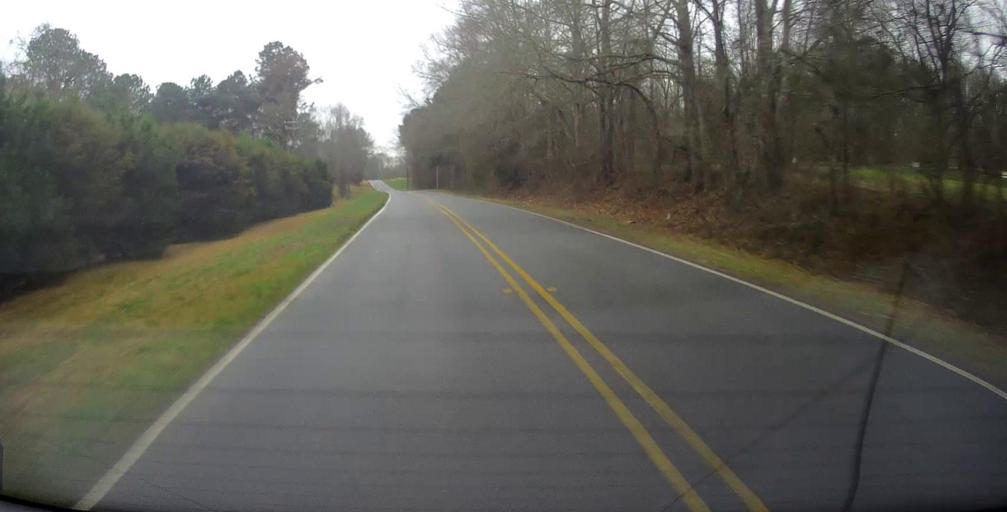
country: US
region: Georgia
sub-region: Pike County
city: Zebulon
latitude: 33.0682
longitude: -84.3273
